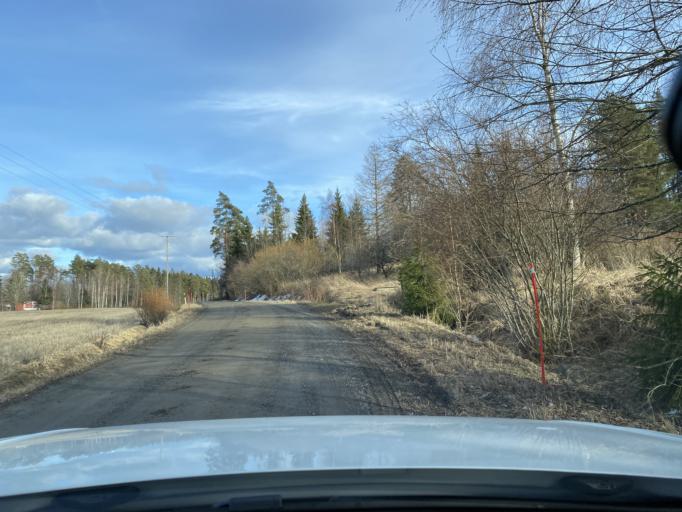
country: FI
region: Pirkanmaa
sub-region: Lounais-Pirkanmaa
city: Punkalaidun
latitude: 61.1438
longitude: 23.2056
